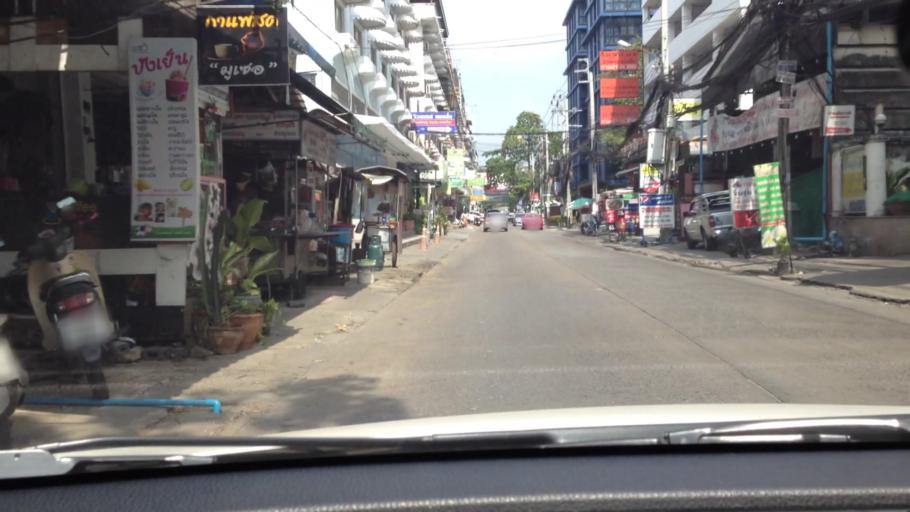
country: TH
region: Bangkok
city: Bang Kapi
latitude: 13.7709
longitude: 100.6322
